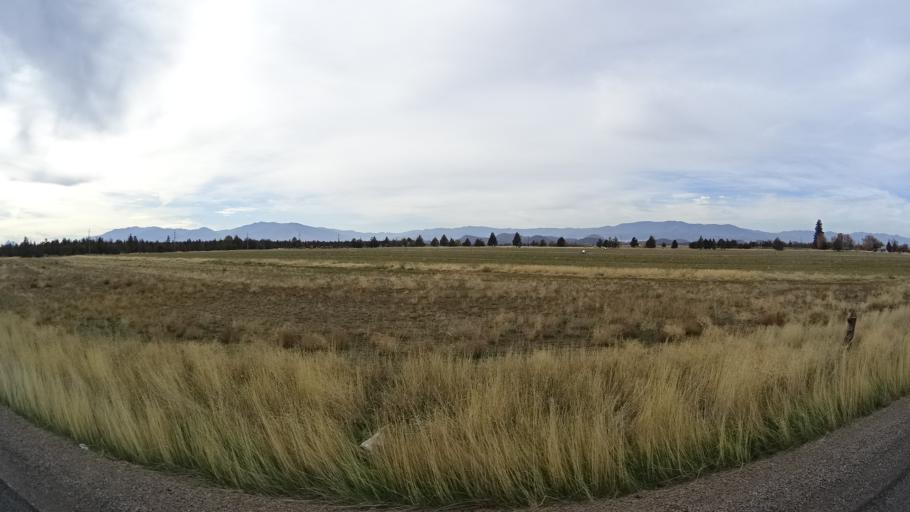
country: US
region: California
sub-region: Siskiyou County
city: Montague
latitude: 41.6211
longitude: -122.3763
